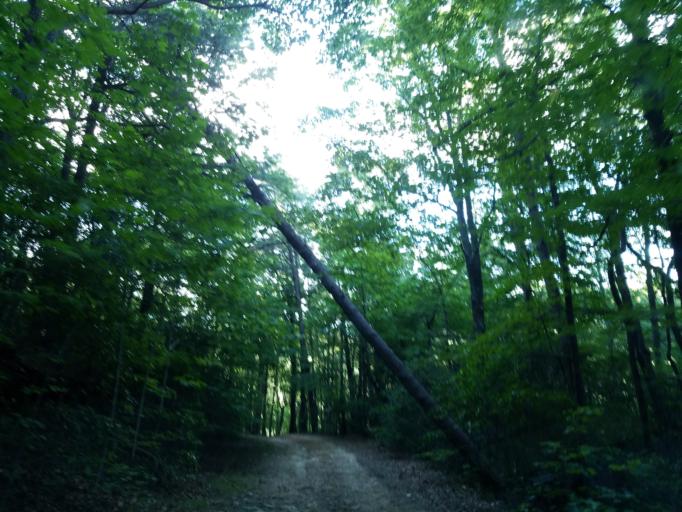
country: US
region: Georgia
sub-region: Dawson County
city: Dawsonville
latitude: 34.6216
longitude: -84.2272
